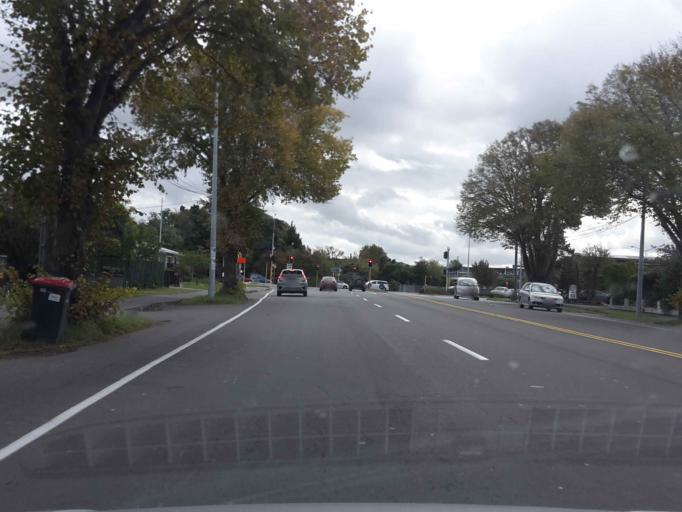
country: NZ
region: Canterbury
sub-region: Christchurch City
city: Christchurch
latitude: -43.4886
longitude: 172.6174
